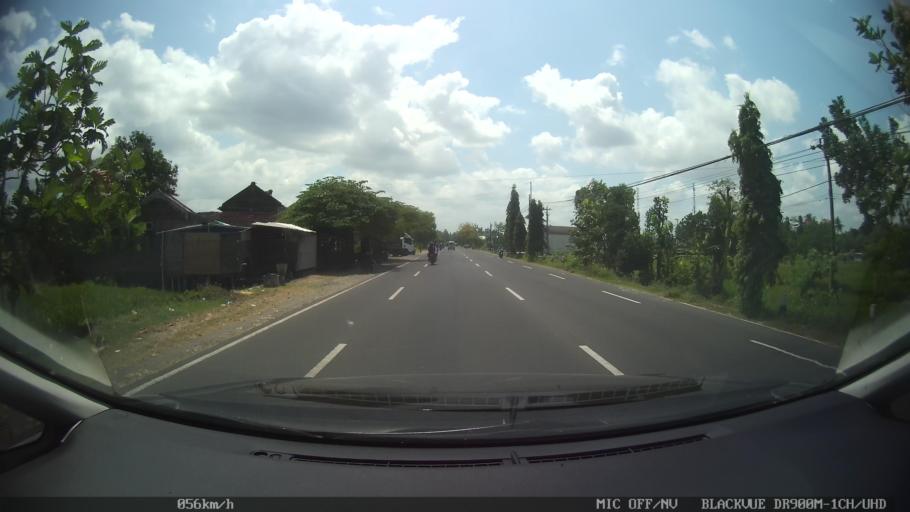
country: ID
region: Daerah Istimewa Yogyakarta
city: Pandak
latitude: -7.9179
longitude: 110.2839
